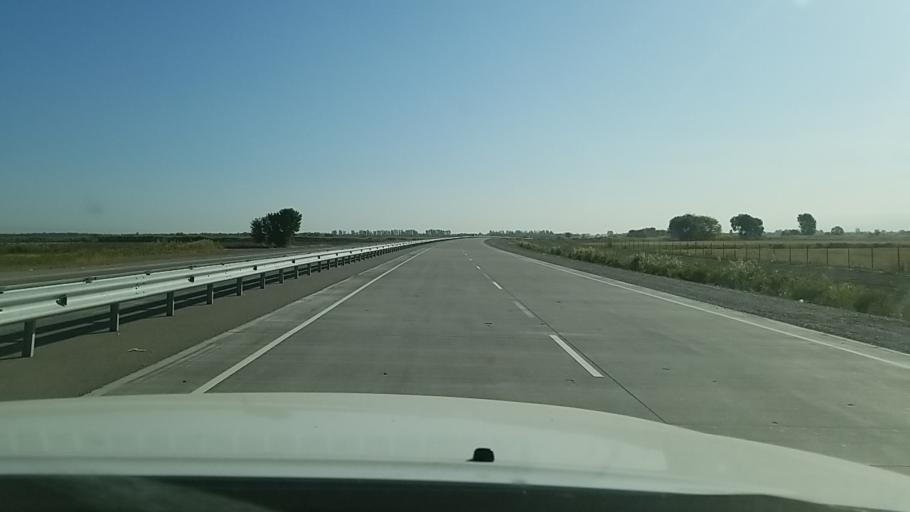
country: KZ
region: Almaty Oblysy
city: Esik
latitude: 43.5042
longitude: 77.3890
